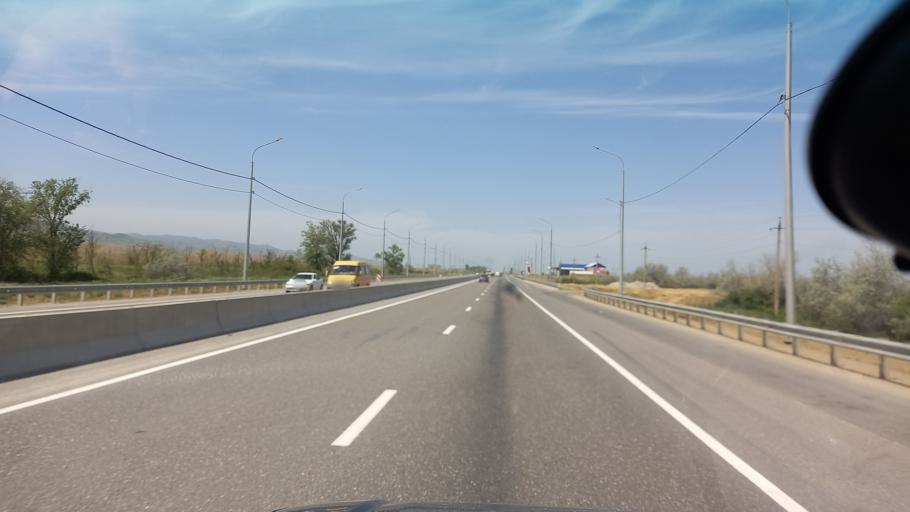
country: RU
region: Dagestan
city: Manas
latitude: 42.7381
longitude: 47.6610
